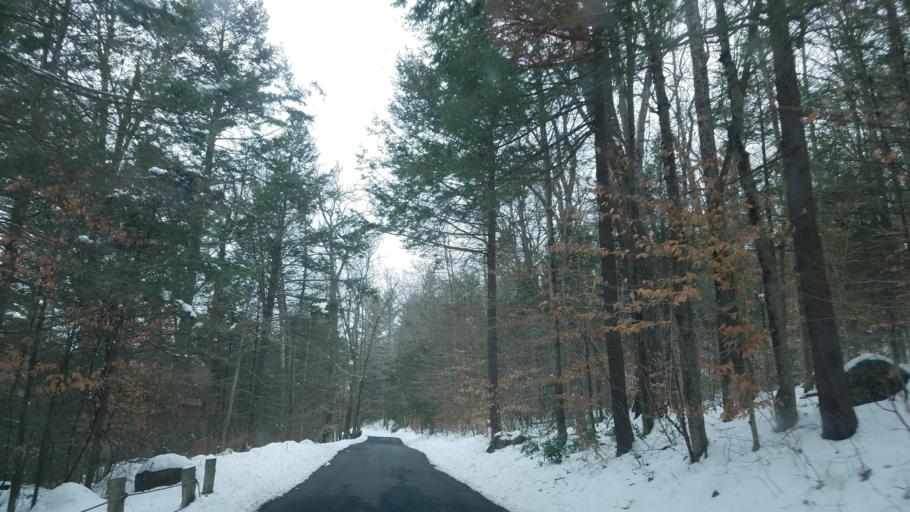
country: US
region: Connecticut
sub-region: Litchfield County
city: Winsted
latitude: 41.9409
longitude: -73.0054
